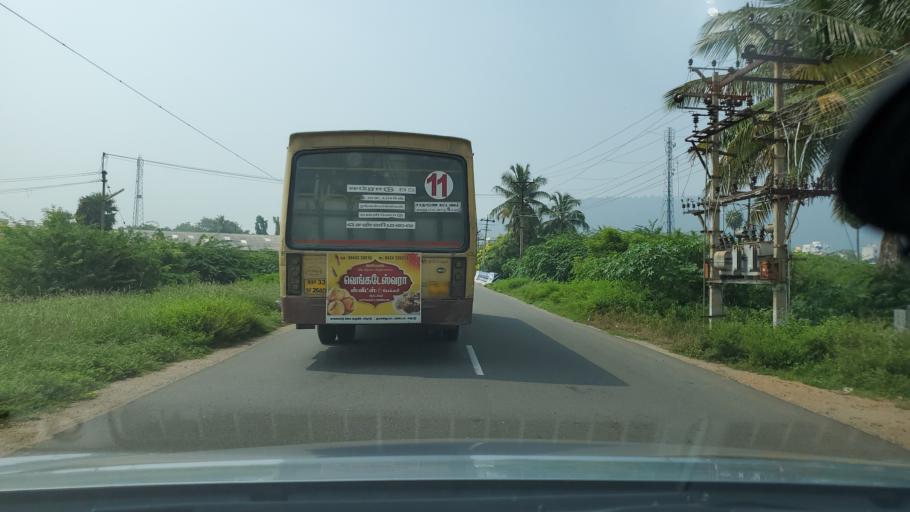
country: IN
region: Tamil Nadu
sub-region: Erode
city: Chennimalai
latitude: 11.1730
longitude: 77.6049
